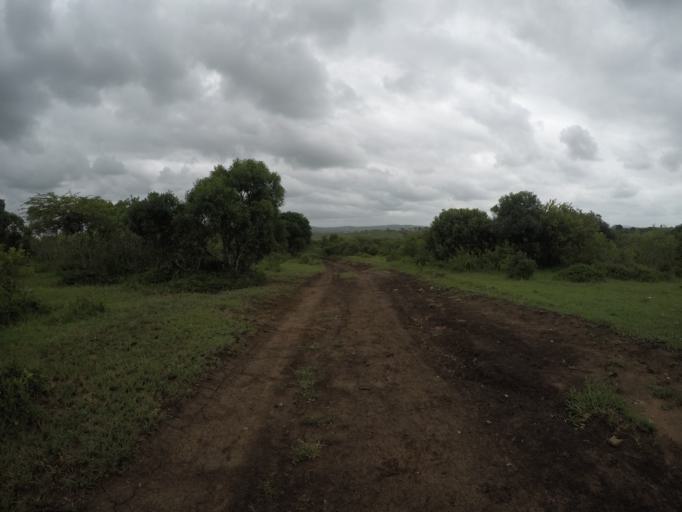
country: ZA
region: KwaZulu-Natal
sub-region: uThungulu District Municipality
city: Empangeni
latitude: -28.5686
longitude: 31.8725
